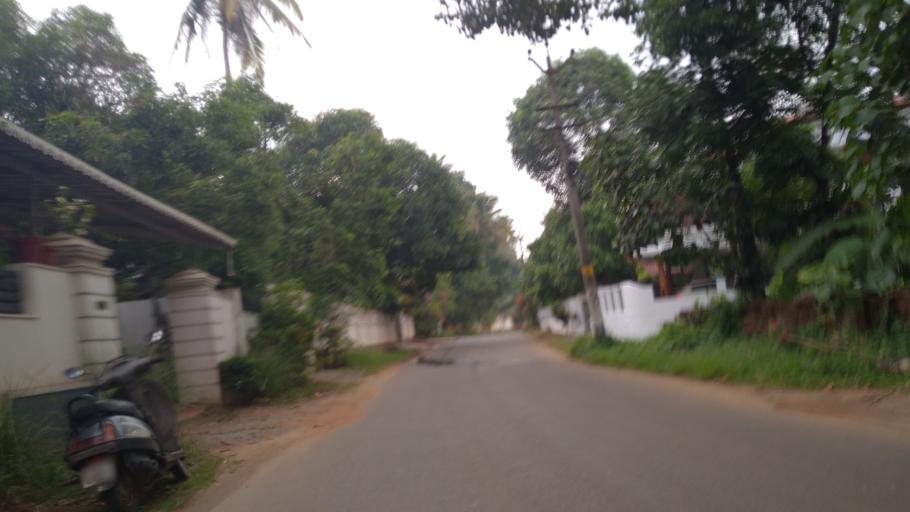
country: IN
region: Kerala
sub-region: Ernakulam
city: Perumbavoor
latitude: 10.0875
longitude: 76.5069
